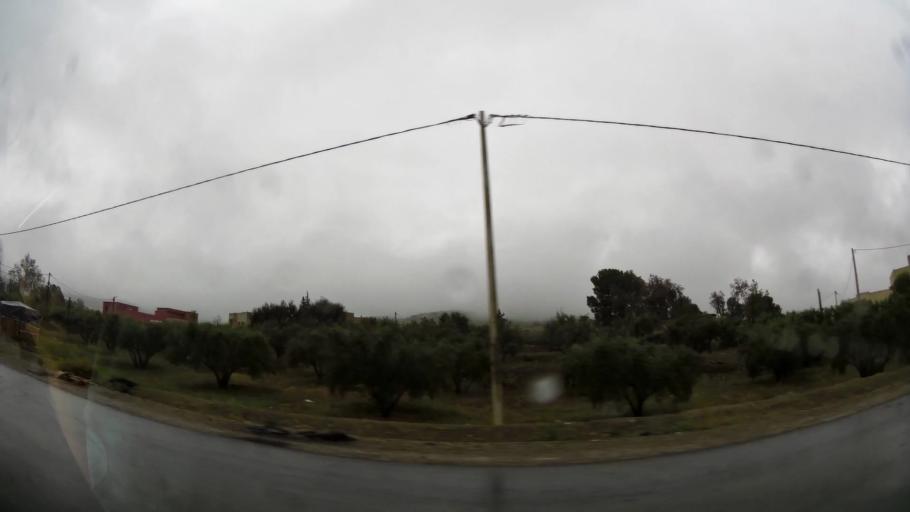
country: MA
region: Taza-Al Hoceima-Taounate
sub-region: Taza
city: Aknoul
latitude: 34.8105
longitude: -3.7358
